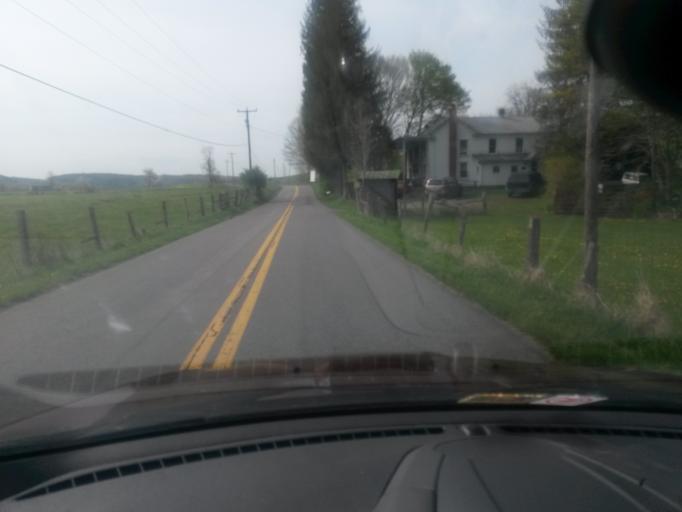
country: US
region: West Virginia
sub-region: Pocahontas County
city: Marlinton
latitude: 38.1208
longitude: -80.2147
